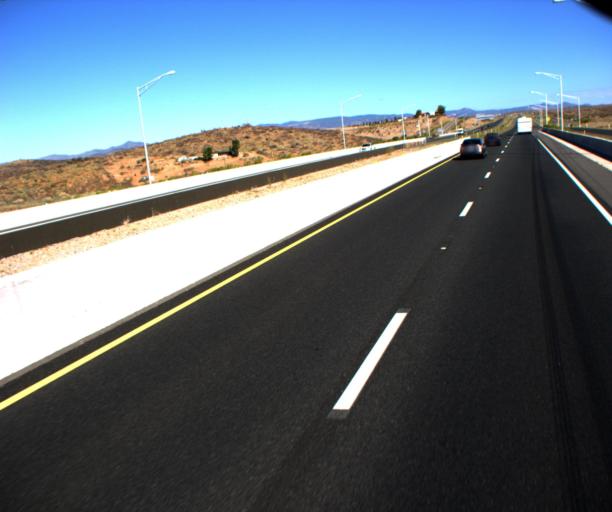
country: US
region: Arizona
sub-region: Yavapai County
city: Cordes Lakes
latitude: 34.3331
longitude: -112.1261
